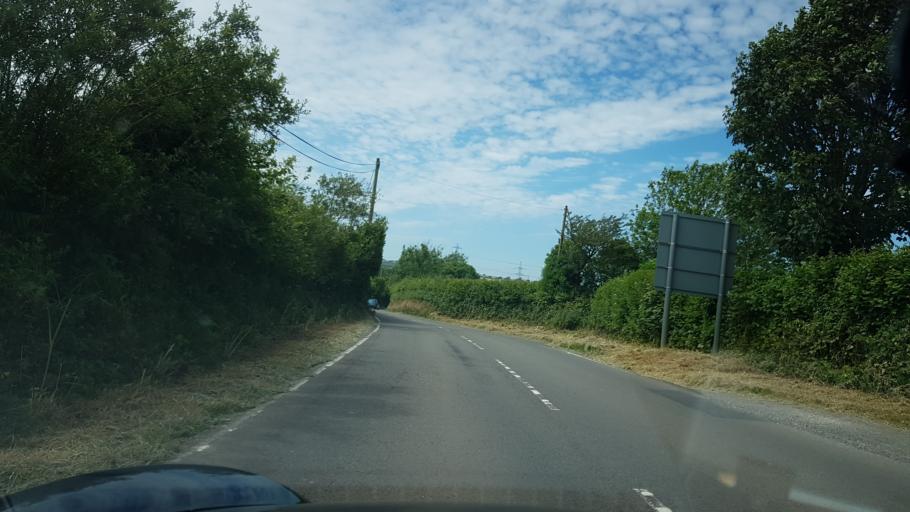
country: GB
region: Wales
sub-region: Carmarthenshire
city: Whitland
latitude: 51.7777
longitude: -4.6095
